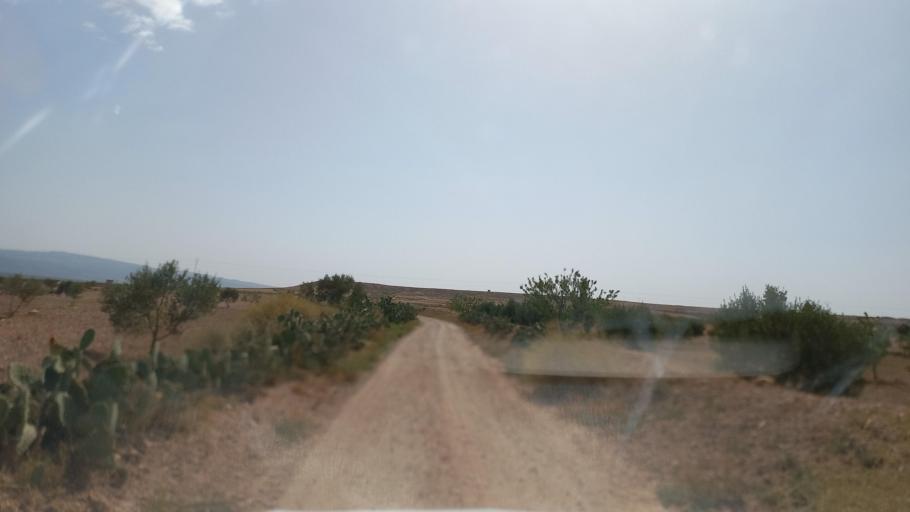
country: TN
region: Al Qasrayn
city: Kasserine
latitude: 35.2749
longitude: 8.9682
